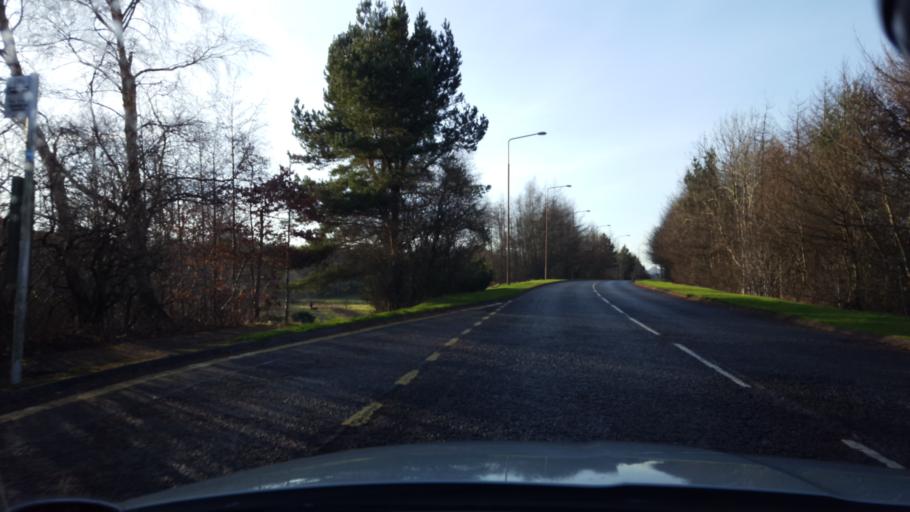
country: GB
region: Scotland
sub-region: West Lothian
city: Livingston
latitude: 55.8747
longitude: -3.5354
